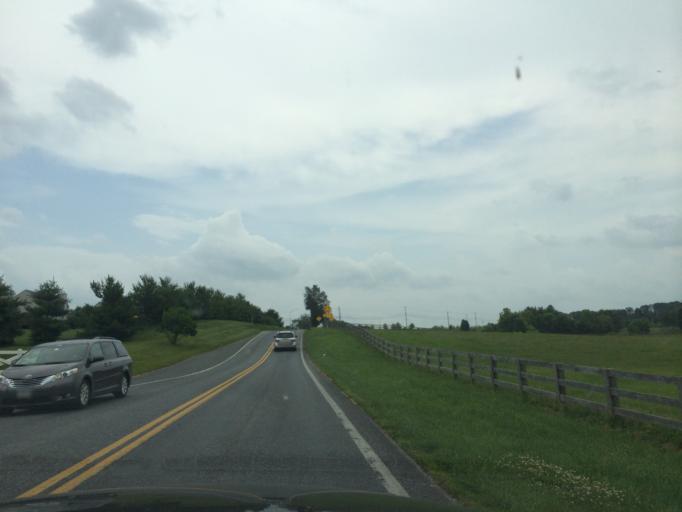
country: US
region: Maryland
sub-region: Carroll County
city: Sykesville
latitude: 39.2790
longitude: -76.9874
